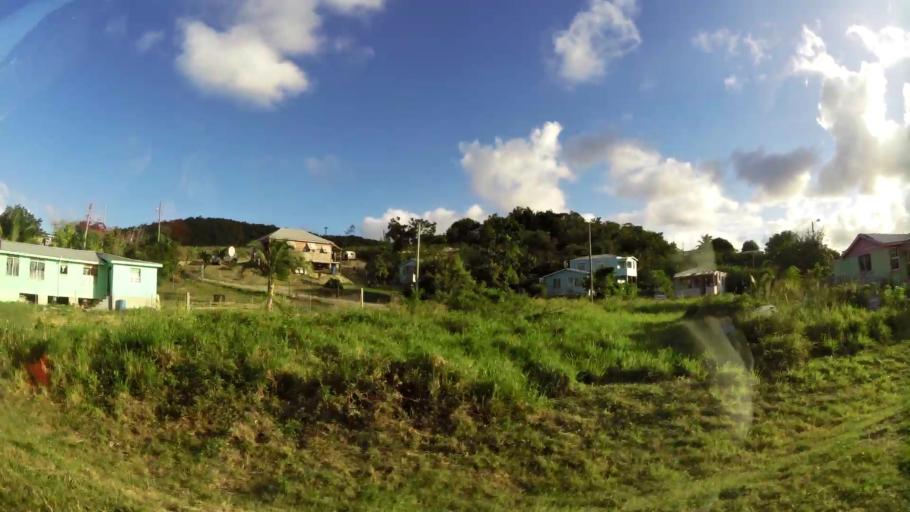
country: AG
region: Saint George
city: Piggotts
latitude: 17.1280
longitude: -61.8044
